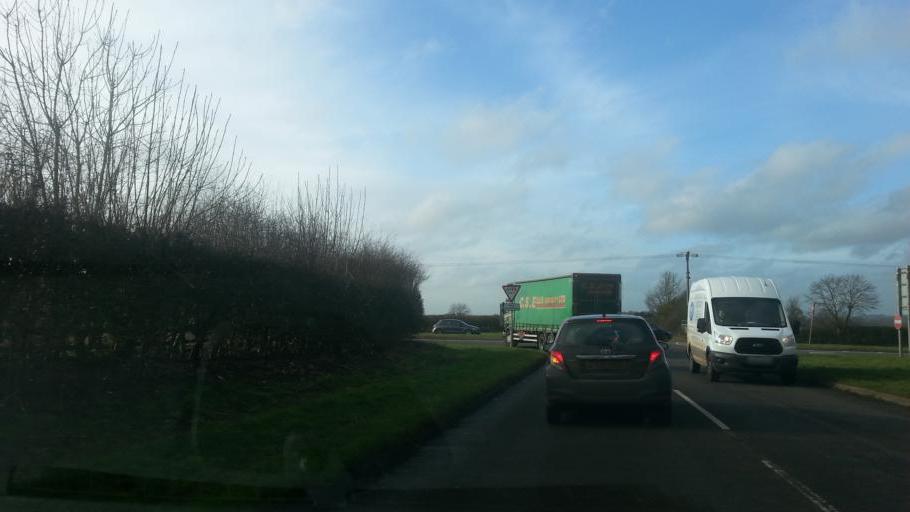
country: GB
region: England
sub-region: District of Rutland
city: Manton
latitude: 52.6308
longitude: -0.7069
